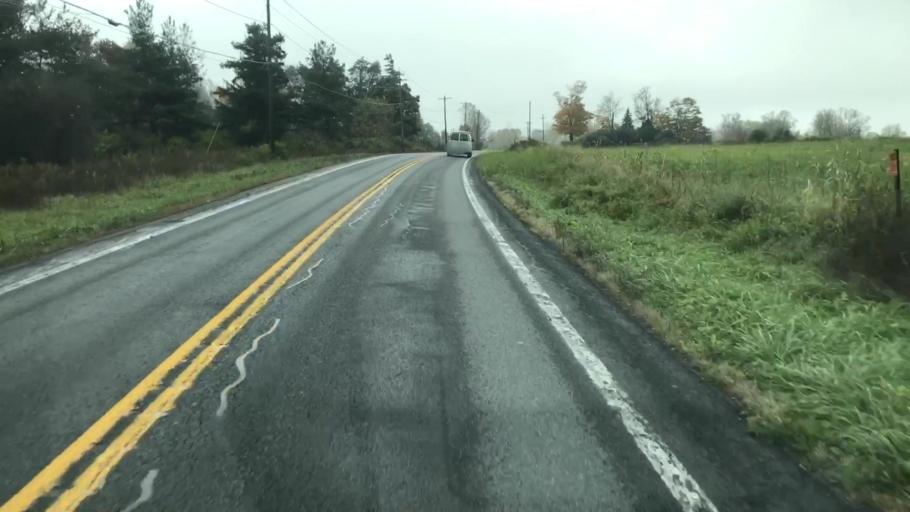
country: US
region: New York
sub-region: Onondaga County
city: Skaneateles
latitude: 42.9744
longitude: -76.4274
